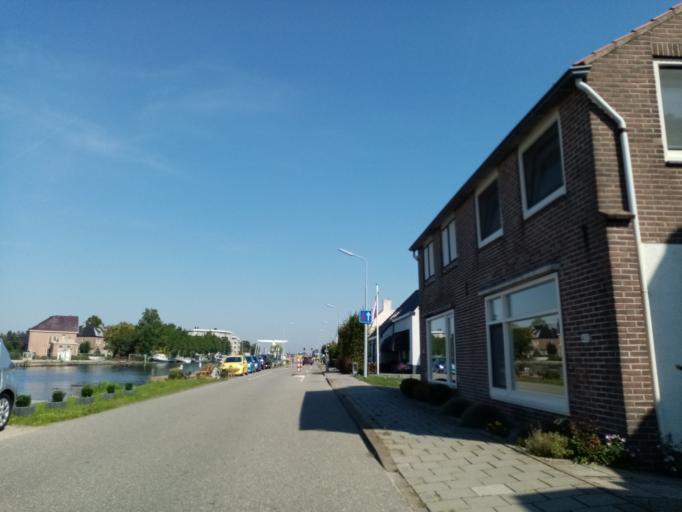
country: NL
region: South Holland
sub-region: Gemeente Lisse
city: Lisse
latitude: 52.2530
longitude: 4.5689
